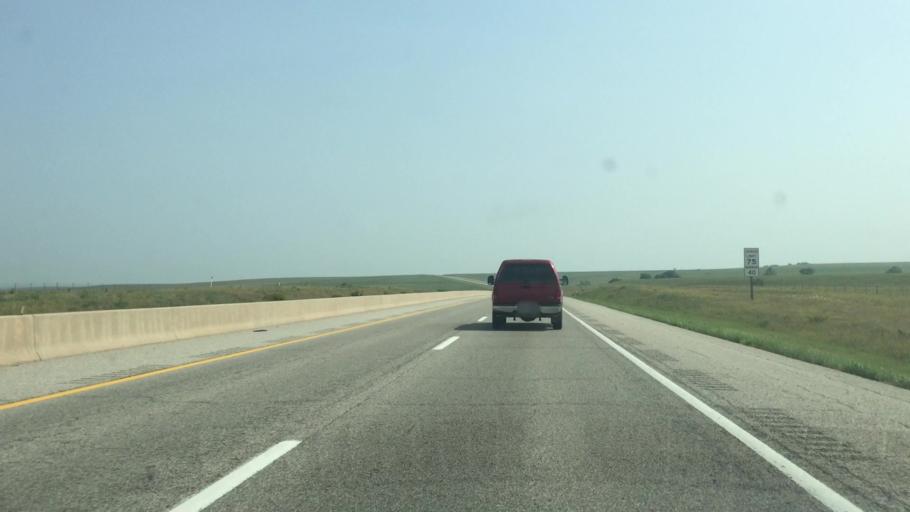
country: US
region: Kansas
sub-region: Chase County
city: Cottonwood Falls
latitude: 38.2845
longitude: -96.3640
